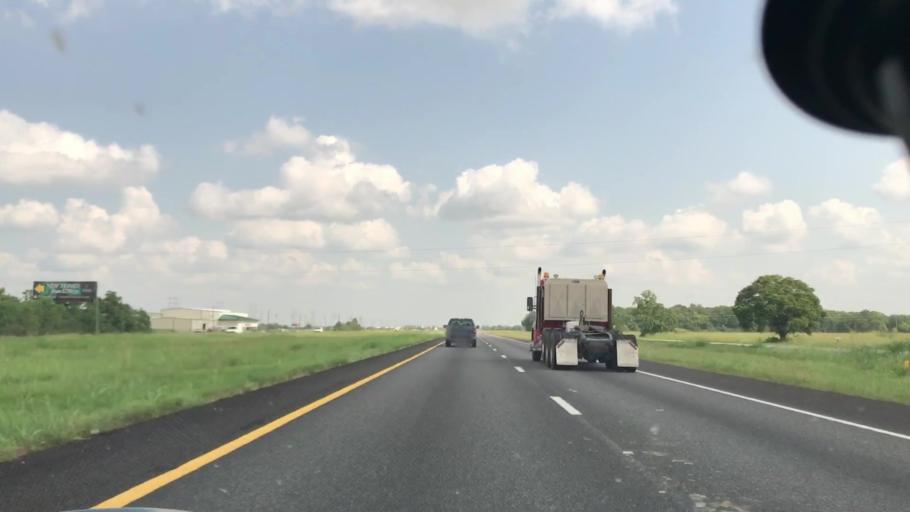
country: US
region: Texas
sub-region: Brazoria County
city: Rosharon
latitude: 29.4004
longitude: -95.4266
